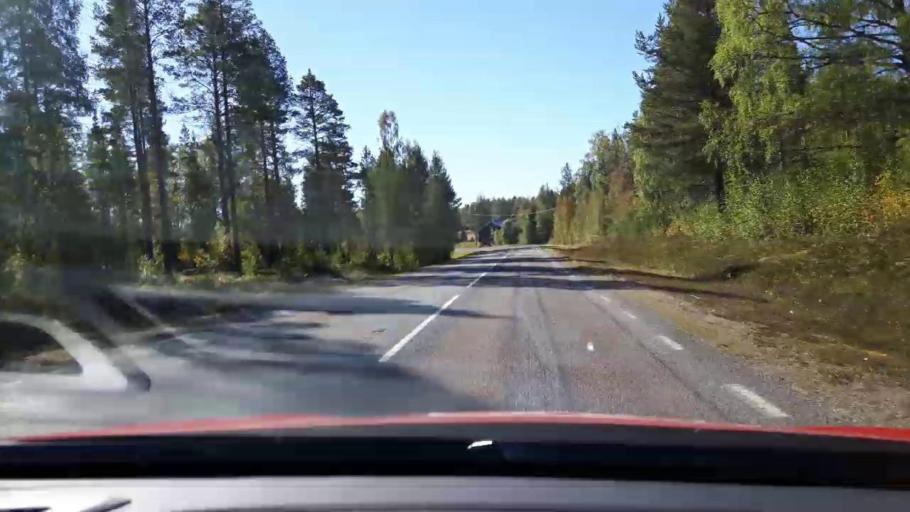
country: SE
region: Jaemtland
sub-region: Harjedalens Kommun
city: Sveg
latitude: 62.1280
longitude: 14.1645
